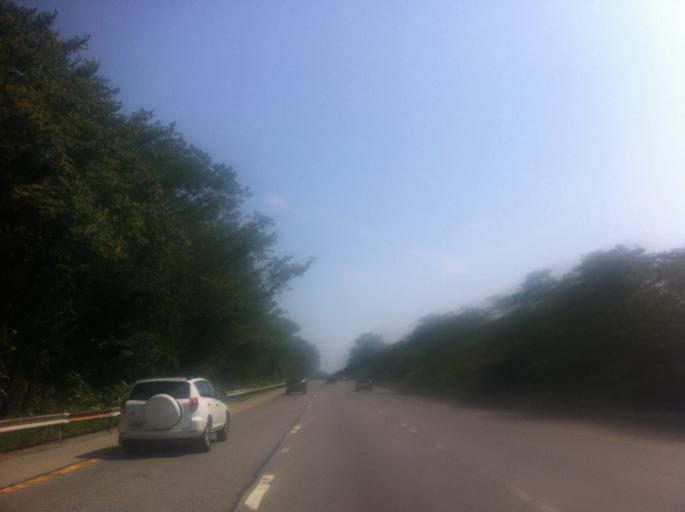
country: US
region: New York
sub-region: Nassau County
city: Bethpage
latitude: 40.7501
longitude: -73.4741
